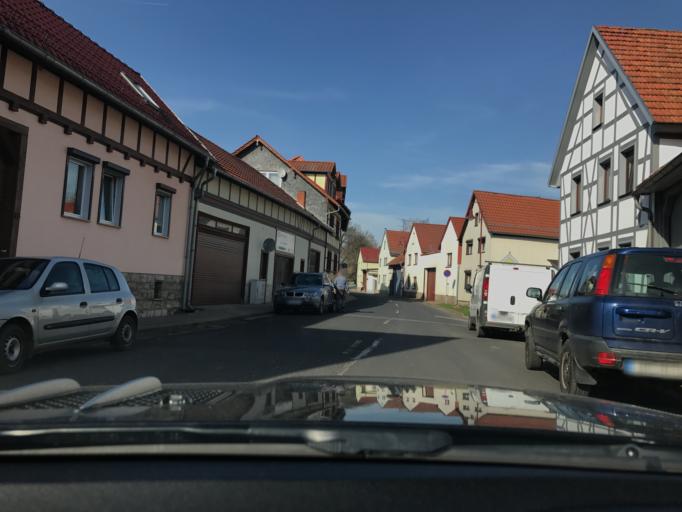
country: DE
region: Thuringia
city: Bothenheilingen
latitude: 51.1862
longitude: 10.6252
